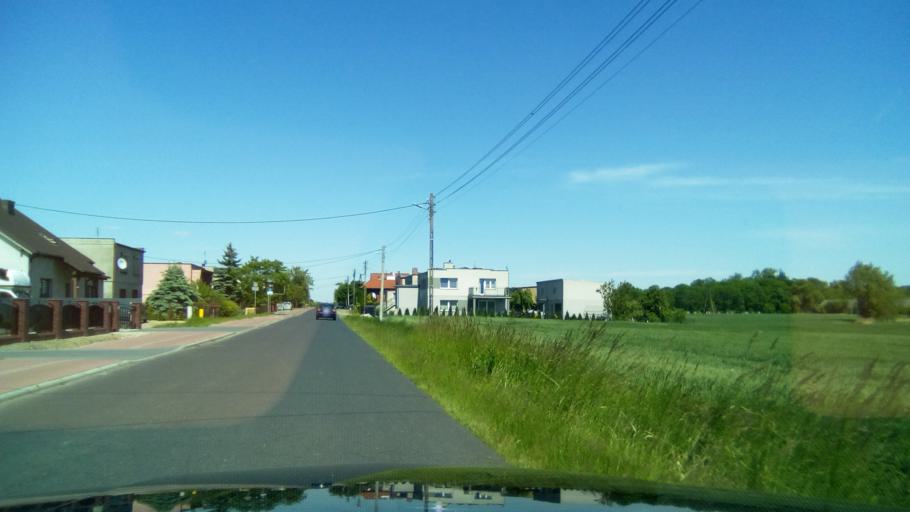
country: PL
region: Greater Poland Voivodeship
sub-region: Powiat gnieznienski
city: Niechanowo
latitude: 52.4616
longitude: 17.6683
